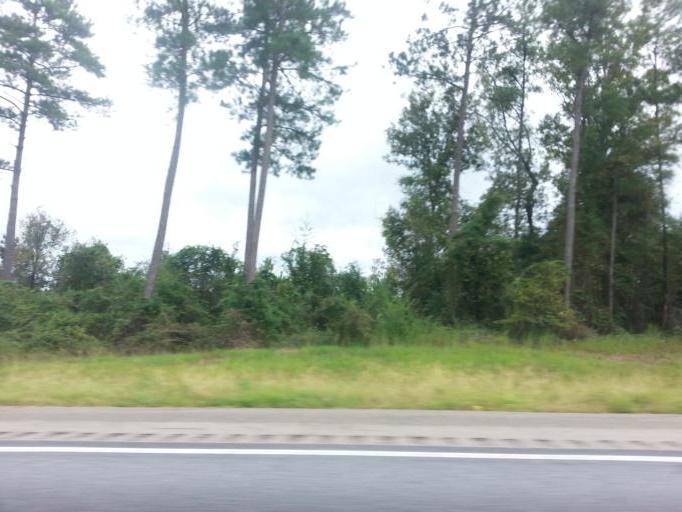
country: US
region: Alabama
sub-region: Escambia County
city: Brewton
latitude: 31.3160
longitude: -87.1486
